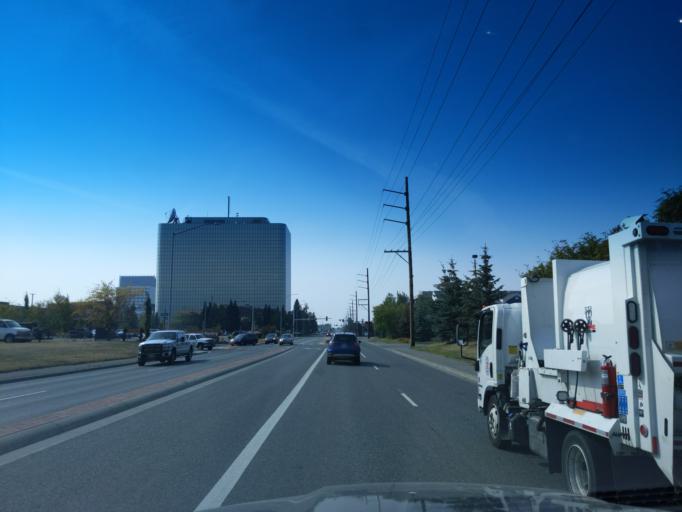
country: US
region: Alaska
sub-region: Anchorage Municipality
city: Anchorage
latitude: 61.1881
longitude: -149.8792
